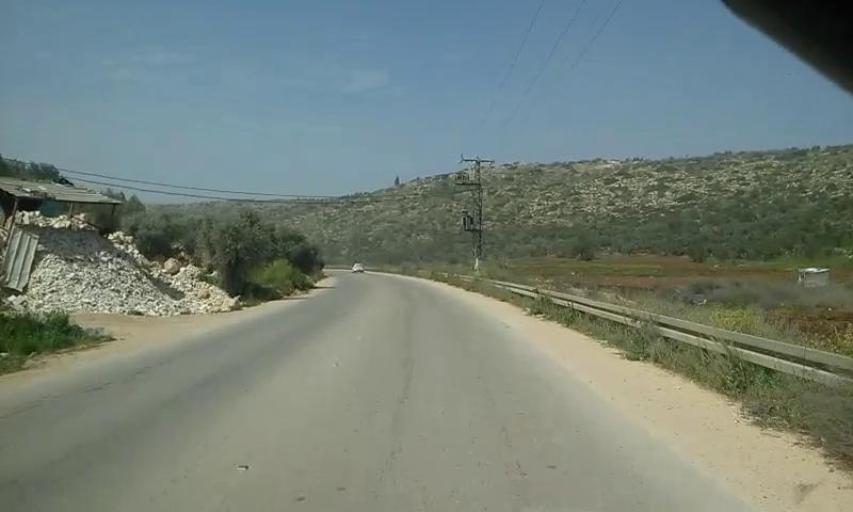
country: PS
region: West Bank
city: Az Zababidah
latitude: 32.4071
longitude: 35.3097
